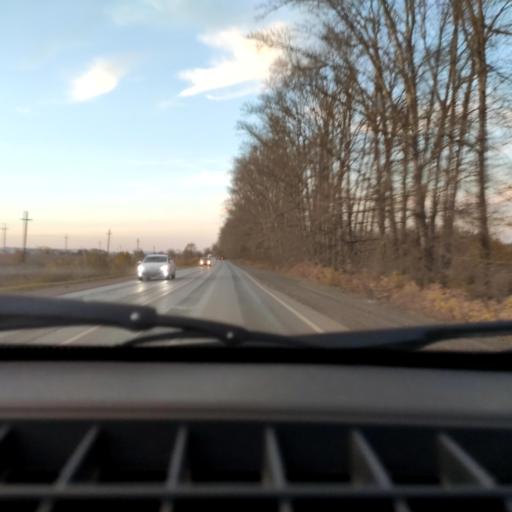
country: RU
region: Bashkortostan
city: Avdon
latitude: 54.7286
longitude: 55.8055
